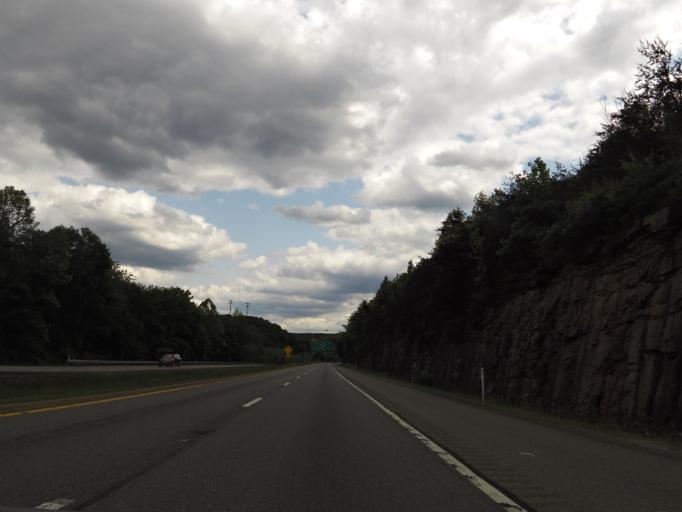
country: US
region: West Virginia
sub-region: Kanawha County
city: Charleston
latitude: 38.3823
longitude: -81.6130
